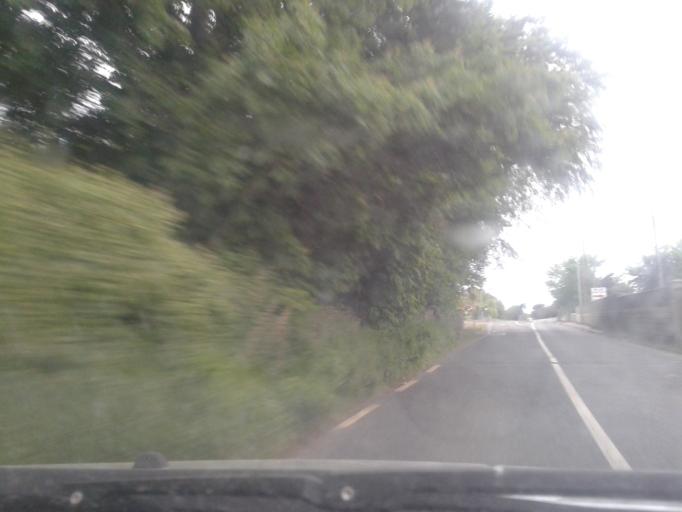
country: IE
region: Leinster
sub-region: Dublin City
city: Finglas
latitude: 53.4165
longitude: -6.3072
